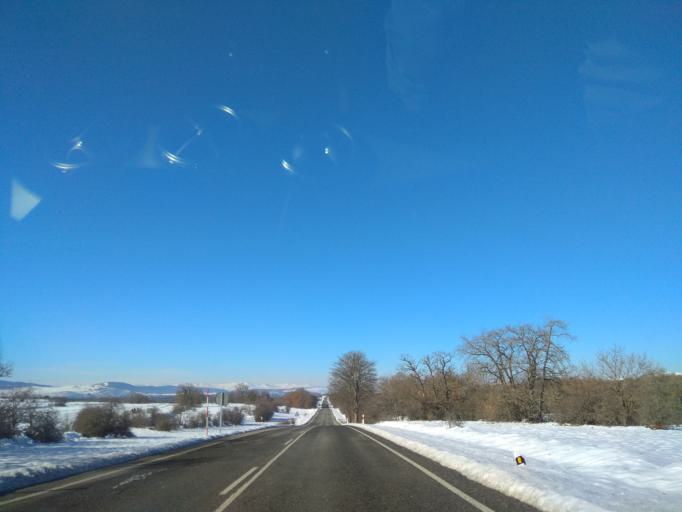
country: ES
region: Cantabria
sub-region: Provincia de Cantabria
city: San Martin de Elines
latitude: 42.9381
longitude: -3.7295
